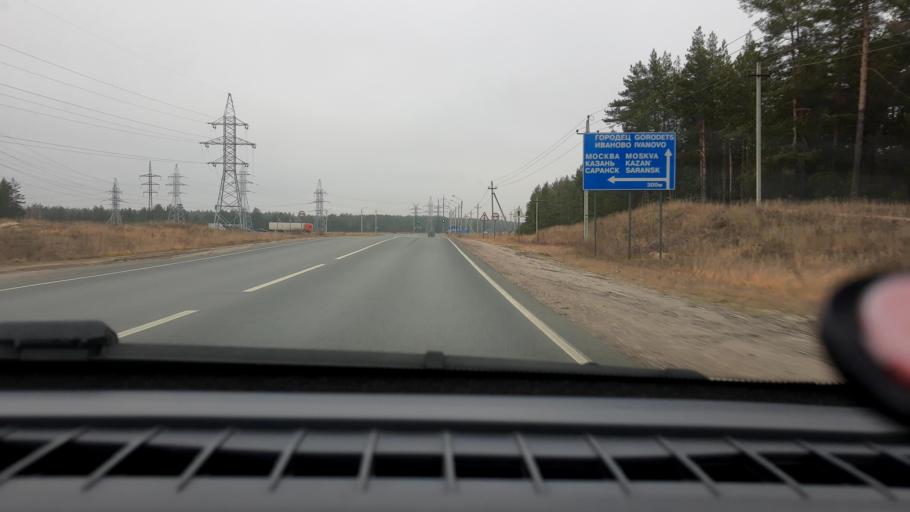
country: RU
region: Nizjnij Novgorod
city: Lukino
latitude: 56.4012
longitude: 43.6595
